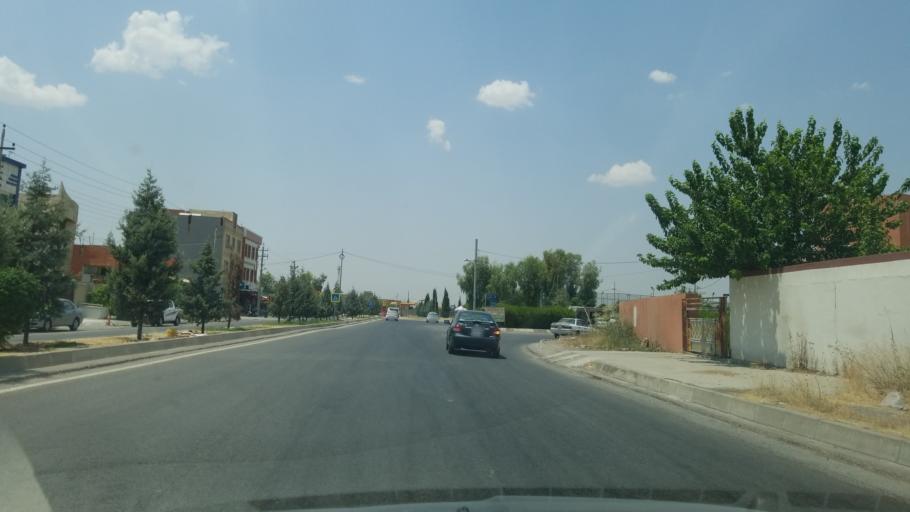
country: IQ
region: Arbil
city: Erbil
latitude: 36.1720
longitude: 44.0576
